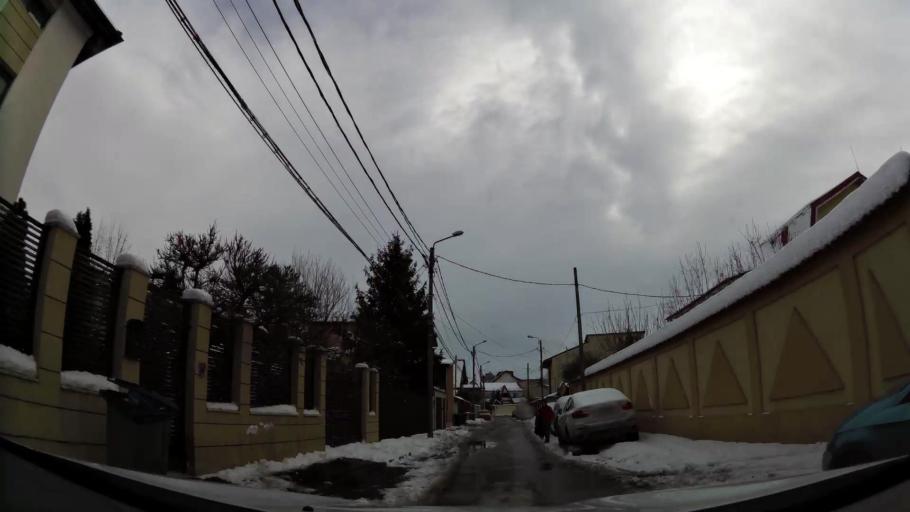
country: RO
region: Bucuresti
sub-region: Municipiul Bucuresti
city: Bucuresti
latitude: 44.3869
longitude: 26.1129
